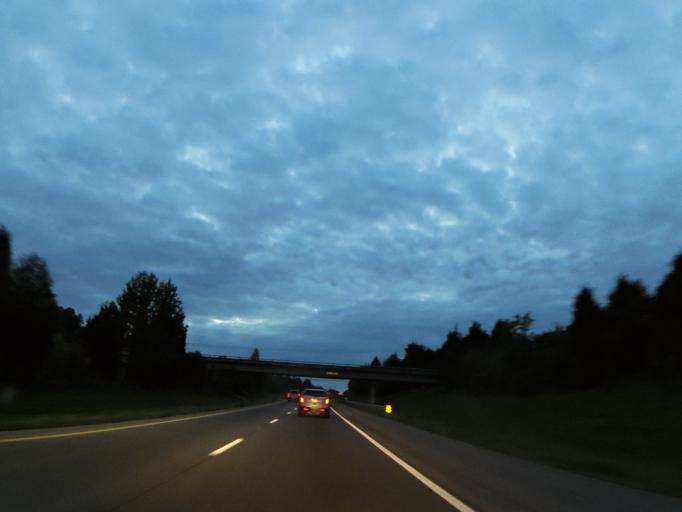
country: US
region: Tennessee
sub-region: Robertson County
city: Ridgetop
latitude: 36.3267
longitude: -86.8855
